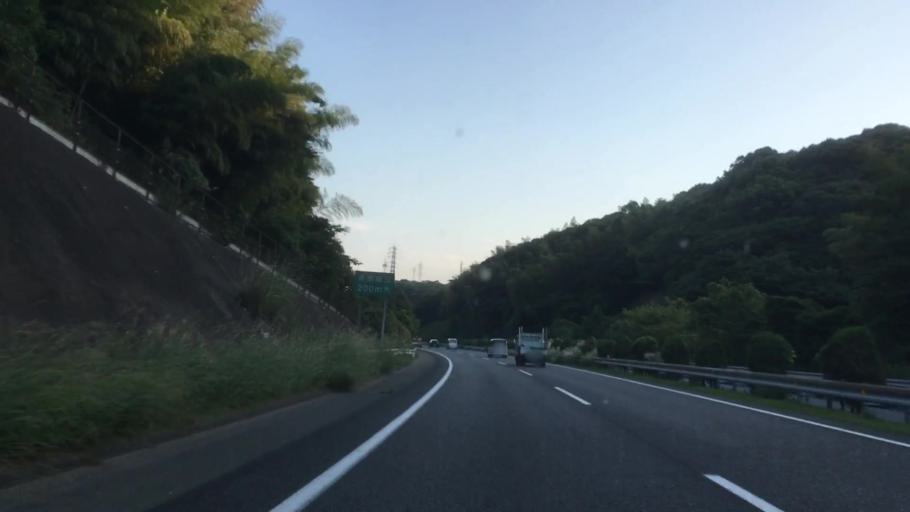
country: JP
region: Yamaguchi
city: Shimonoseki
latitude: 33.9026
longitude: 130.9714
